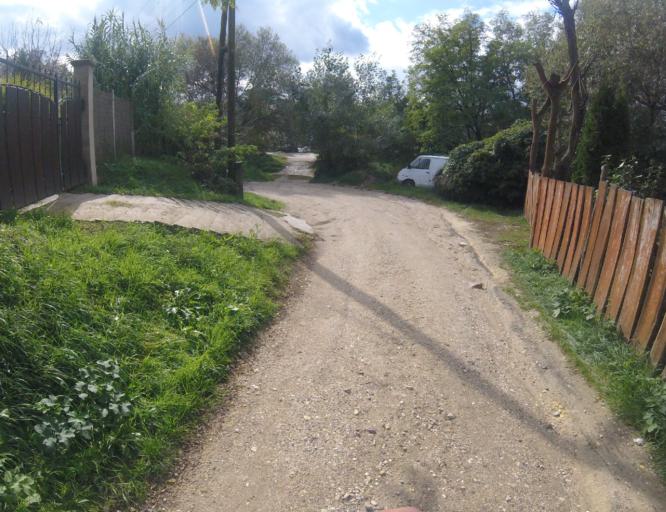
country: HU
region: Pest
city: Csobanka
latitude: 47.6476
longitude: 18.9603
